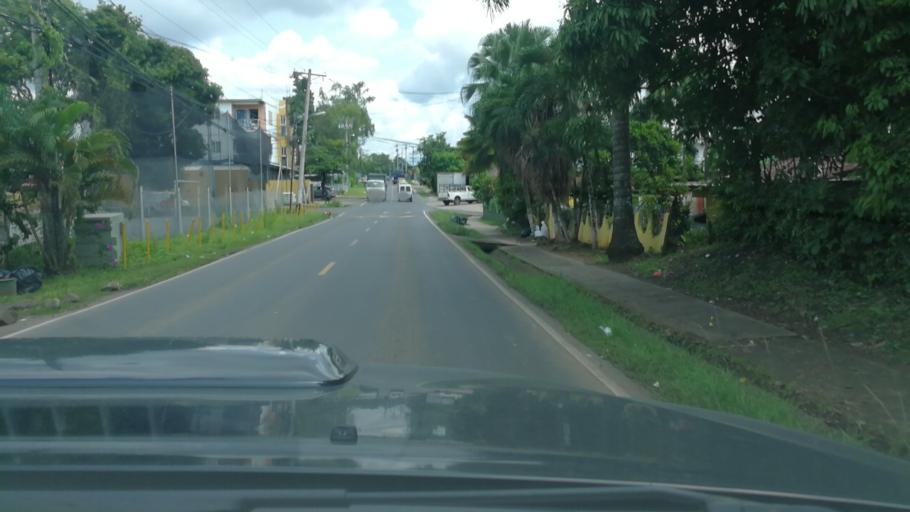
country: PA
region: Panama
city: Tocumen
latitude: 9.0725
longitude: -79.4269
